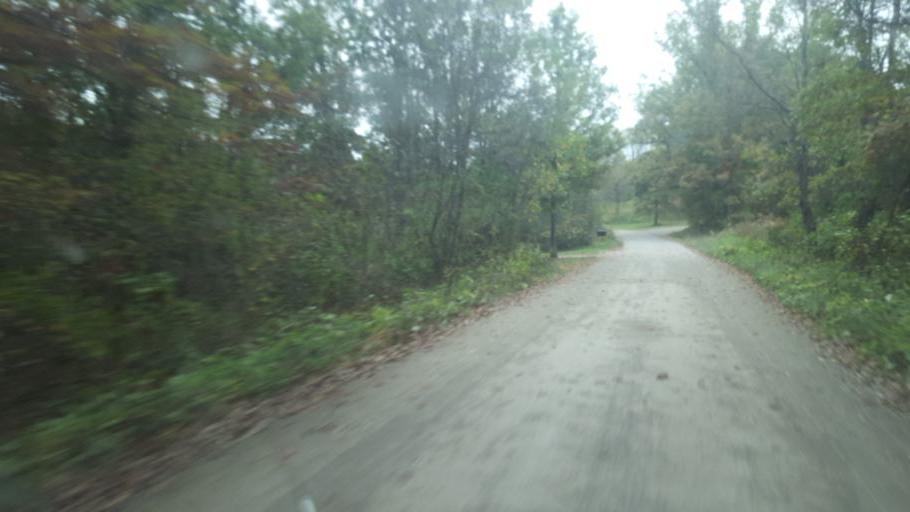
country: US
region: Ohio
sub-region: Harrison County
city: Cadiz
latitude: 40.3821
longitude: -81.0434
